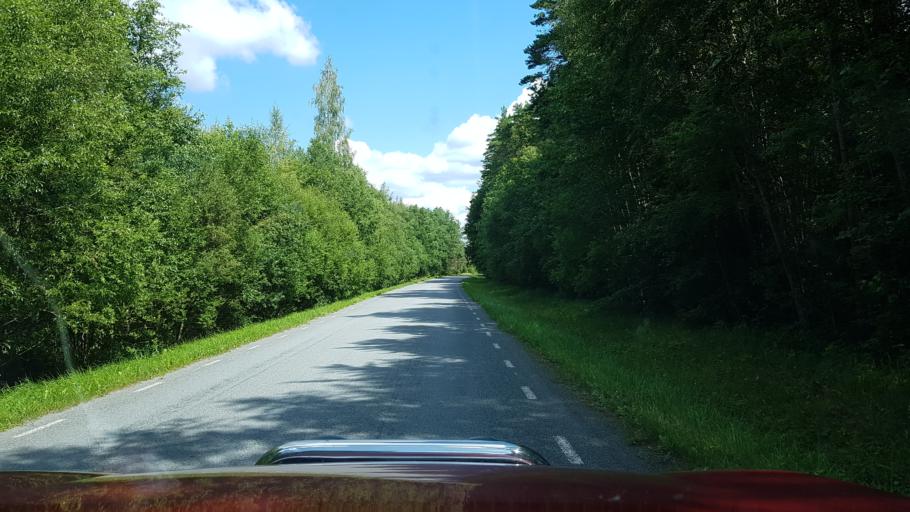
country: EE
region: Raplamaa
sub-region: Maerjamaa vald
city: Marjamaa
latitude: 58.7676
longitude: 24.4368
